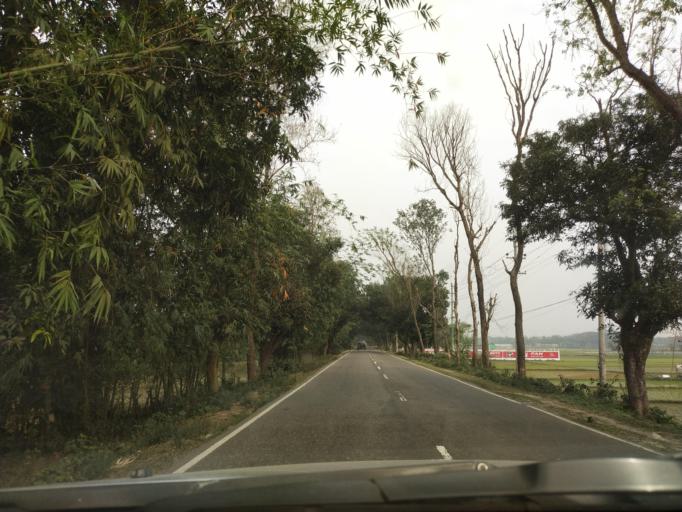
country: BD
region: Dhaka
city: Narsingdi
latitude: 24.0017
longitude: 90.7375
